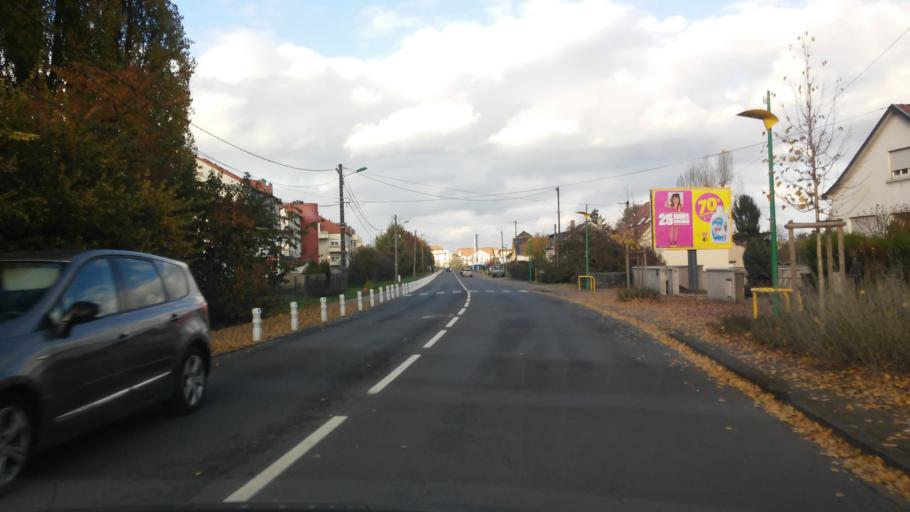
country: FR
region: Lorraine
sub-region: Departement de la Moselle
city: Talange
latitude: 49.2231
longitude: 6.1653
